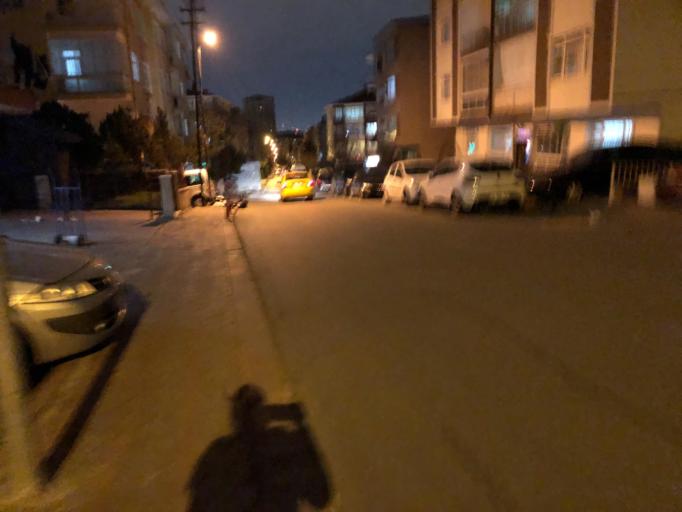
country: TR
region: Ankara
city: Ankara
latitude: 39.9806
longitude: 32.8347
